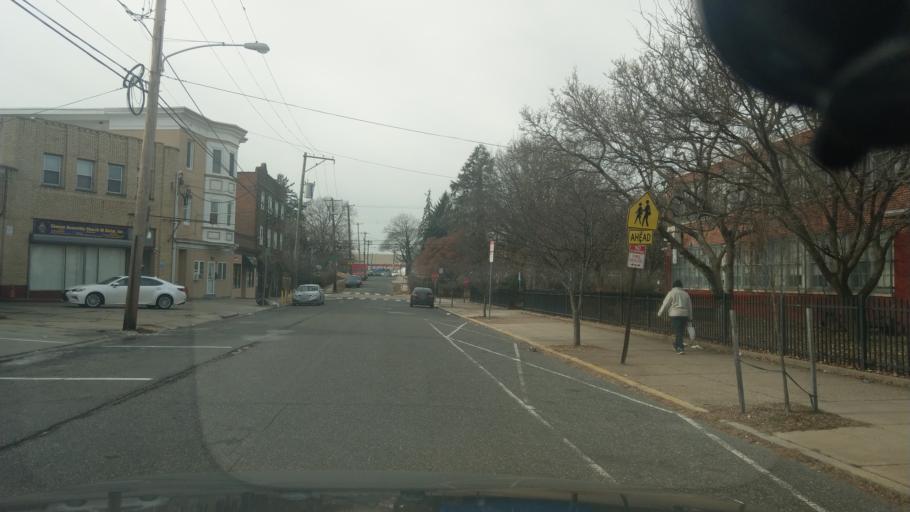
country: US
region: Pennsylvania
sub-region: Montgomery County
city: Wyncote
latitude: 40.0549
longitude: -75.1381
